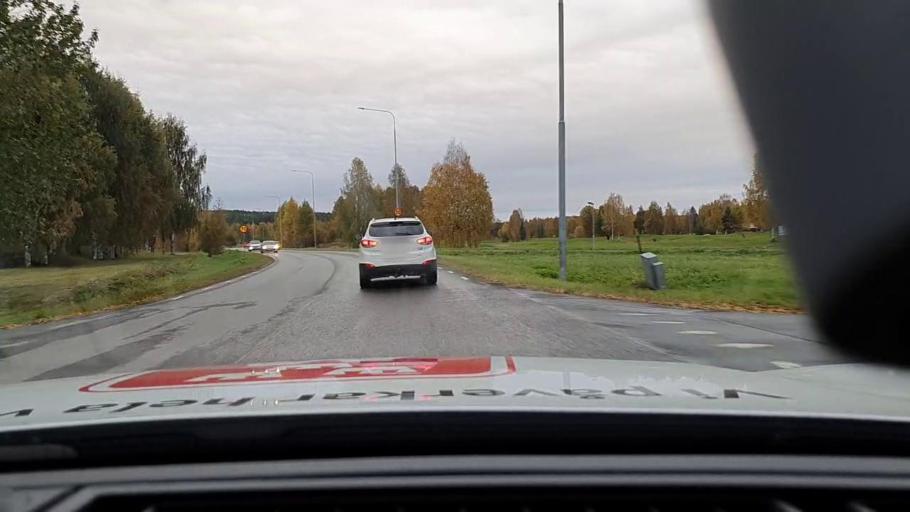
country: SE
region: Norrbotten
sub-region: Bodens Kommun
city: Saevast
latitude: 65.7576
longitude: 21.7455
